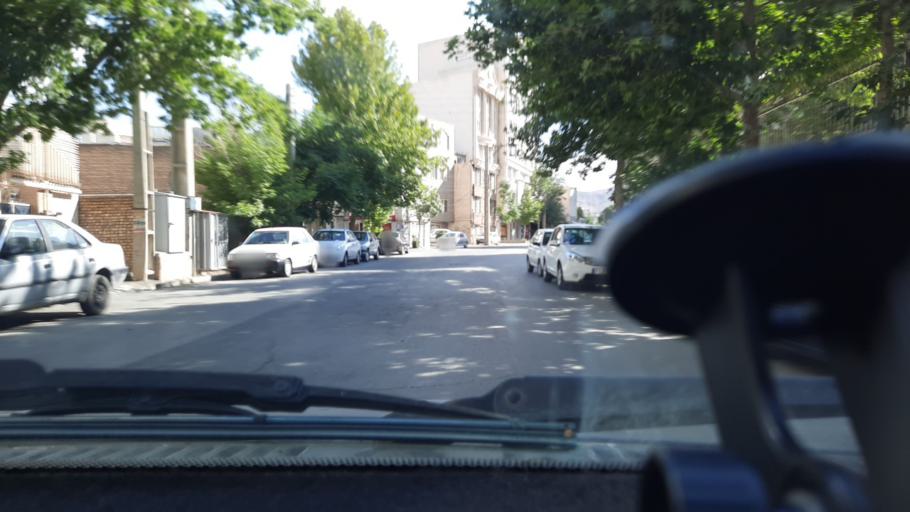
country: IR
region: Markazi
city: Arak
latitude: 34.0788
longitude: 49.6877
